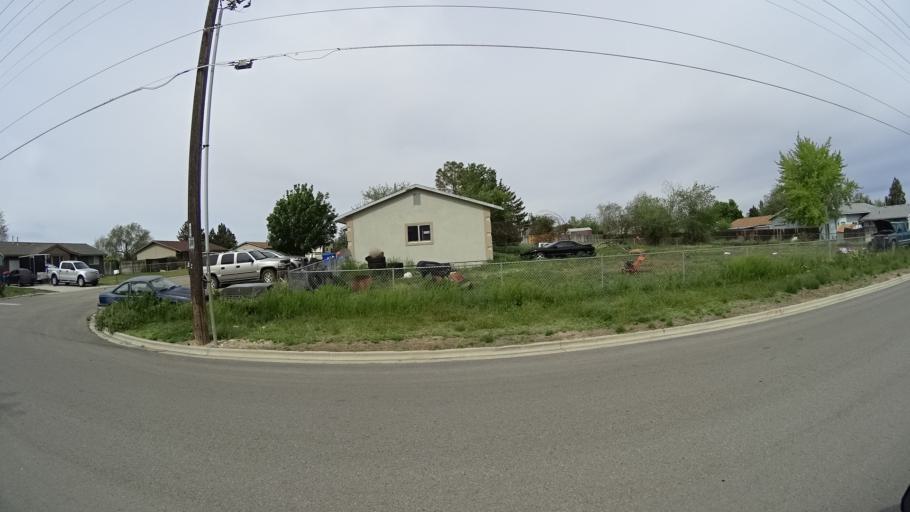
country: US
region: Idaho
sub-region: Ada County
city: Meridian
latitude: 43.5311
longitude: -116.3145
